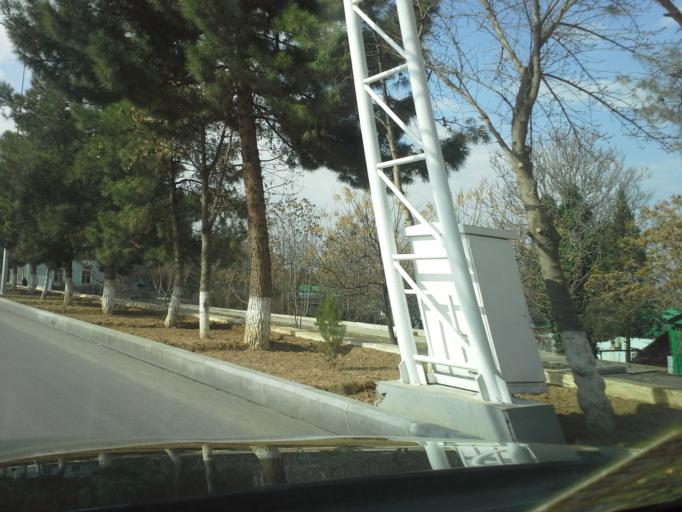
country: TM
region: Ahal
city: Ashgabat
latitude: 37.9536
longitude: 58.3319
